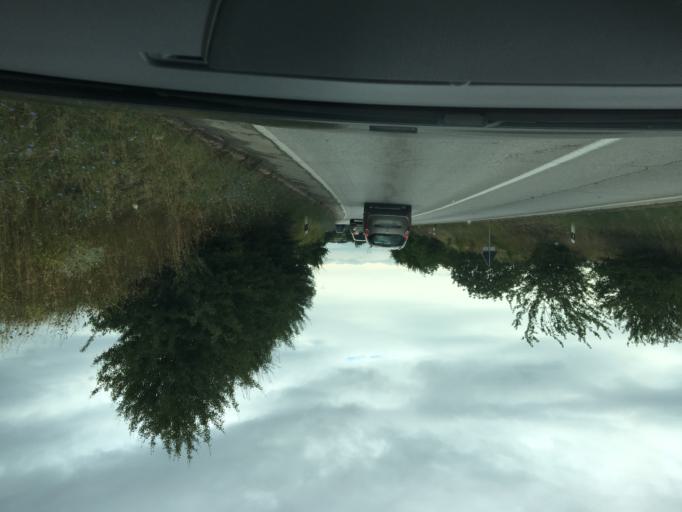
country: MK
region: Staro Nagoricane
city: Staro Nagorichane
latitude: 42.1736
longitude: 21.7921
